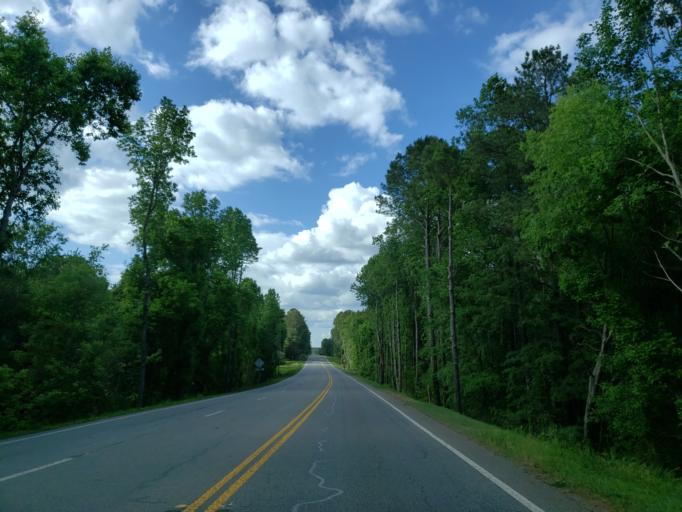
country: US
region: Georgia
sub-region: Bartow County
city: Cartersville
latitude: 34.2511
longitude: -84.8576
